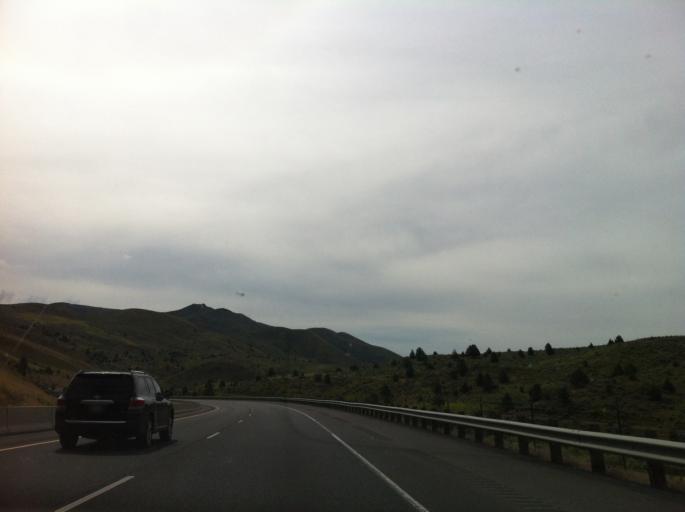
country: US
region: Idaho
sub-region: Washington County
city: Weiser
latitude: 44.5207
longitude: -117.3840
